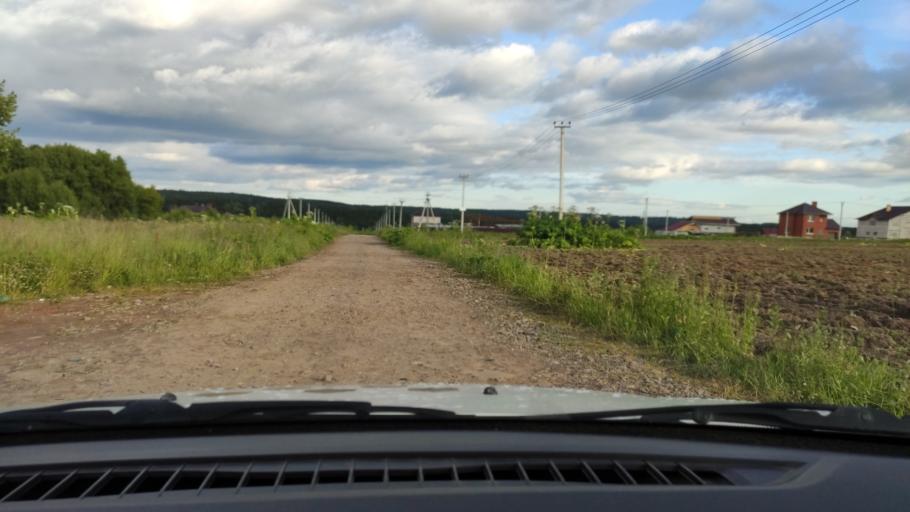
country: RU
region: Perm
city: Perm
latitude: 58.0363
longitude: 56.3785
